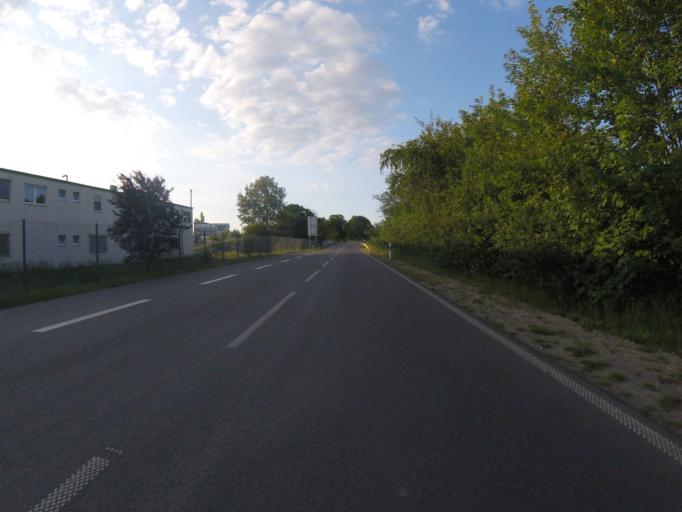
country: DE
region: Brandenburg
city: Mittenwalde
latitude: 52.2352
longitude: 13.5509
